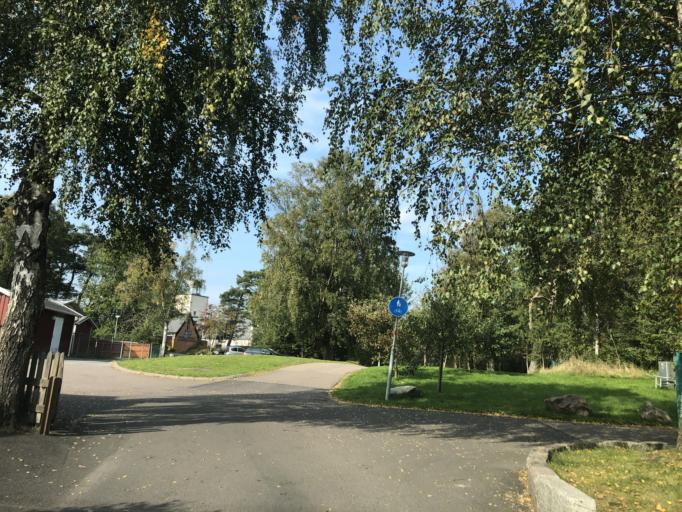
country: SE
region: Vaestra Goetaland
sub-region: Goteborg
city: Majorna
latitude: 57.6525
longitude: 11.8957
